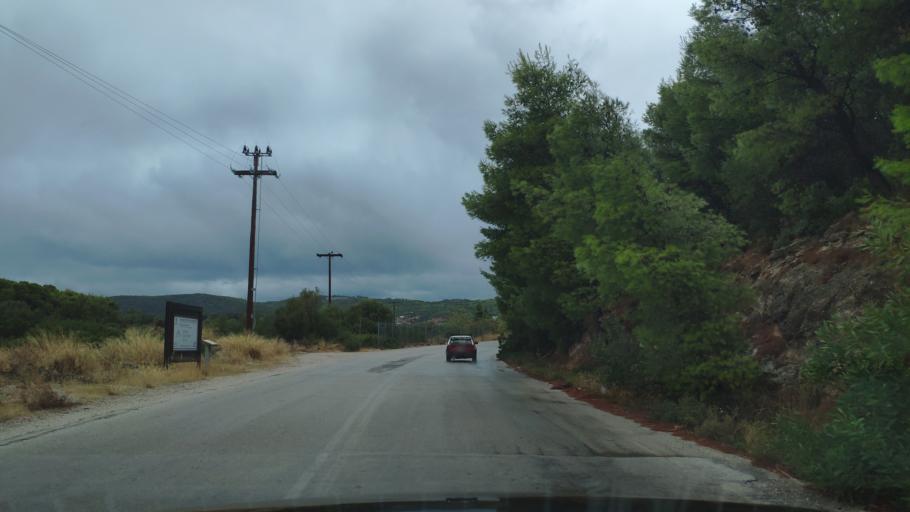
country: GR
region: Peloponnese
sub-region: Nomos Korinthias
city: Perachora
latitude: 38.0127
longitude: 22.9453
